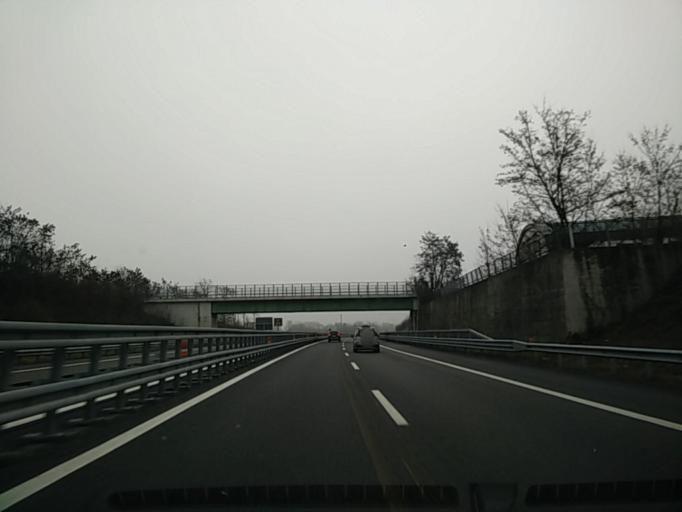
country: IT
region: Piedmont
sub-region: Provincia di Asti
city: Asti
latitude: 44.9167
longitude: 8.1914
